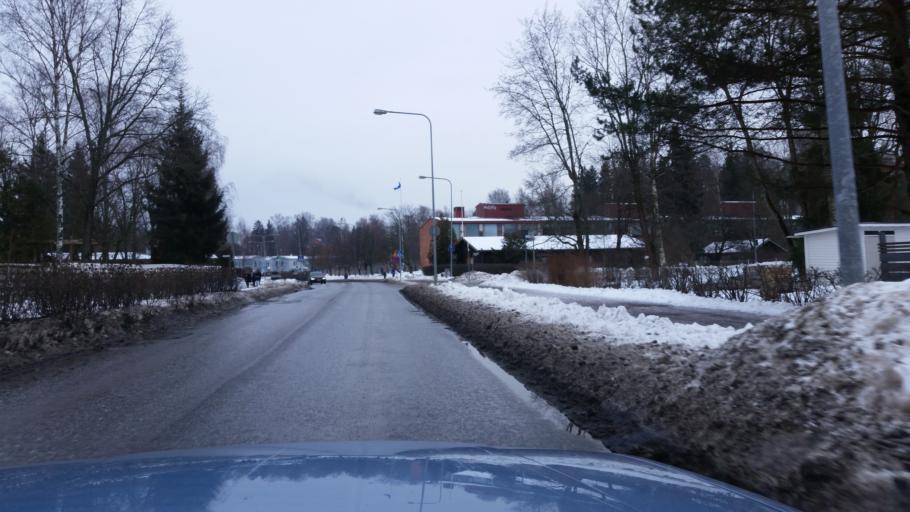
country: FI
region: Uusimaa
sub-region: Helsinki
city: Vantaa
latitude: 60.2713
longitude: 25.0487
